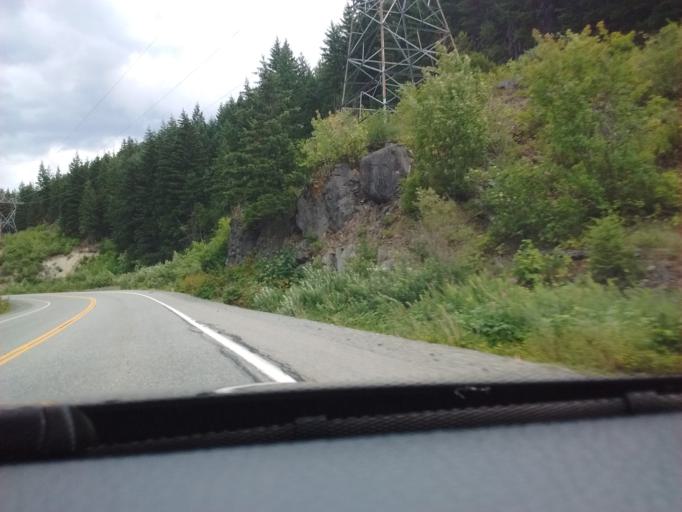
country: CA
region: British Columbia
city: Pemberton
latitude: 50.2990
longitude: -122.8137
